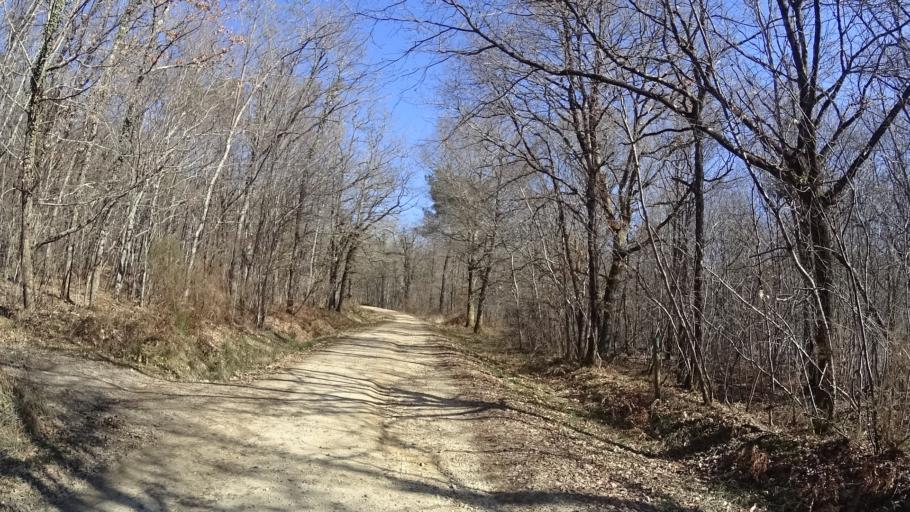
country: FR
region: Aquitaine
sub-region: Departement de la Dordogne
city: Montpon-Menesterol
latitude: 45.0954
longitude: 0.1913
